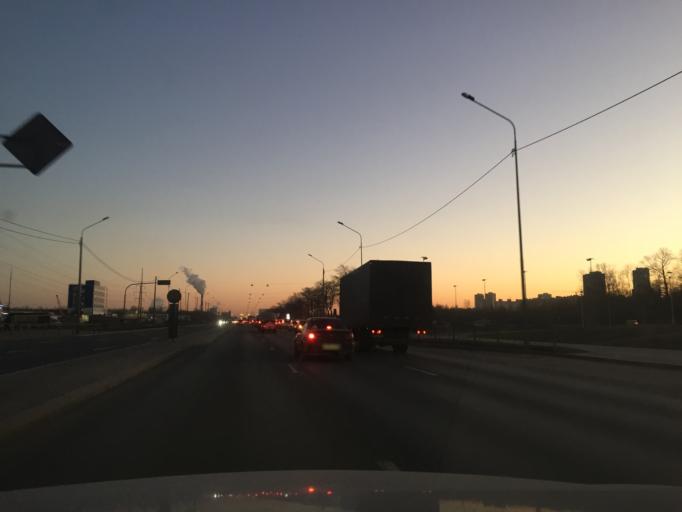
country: RU
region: St.-Petersburg
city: Obukhovo
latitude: 59.8584
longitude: 30.4212
